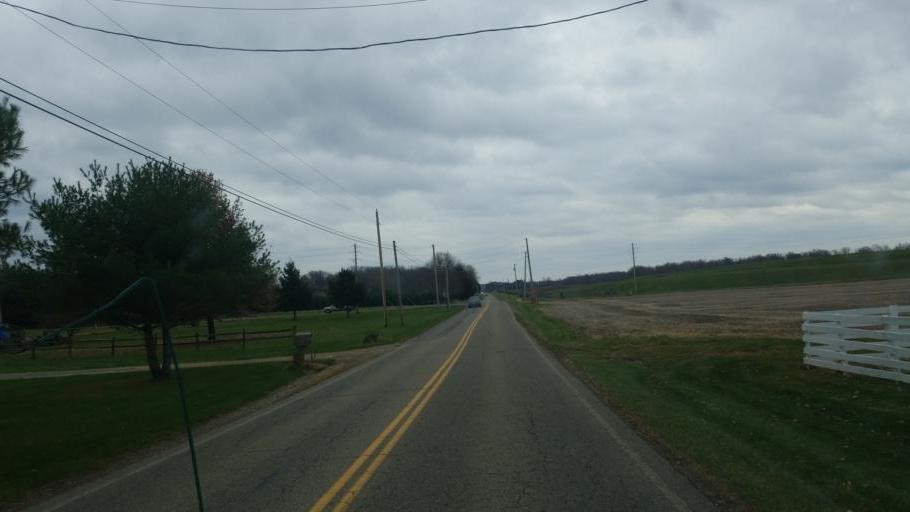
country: US
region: Ohio
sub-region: Knox County
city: Fredericktown
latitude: 40.4604
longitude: -82.5204
